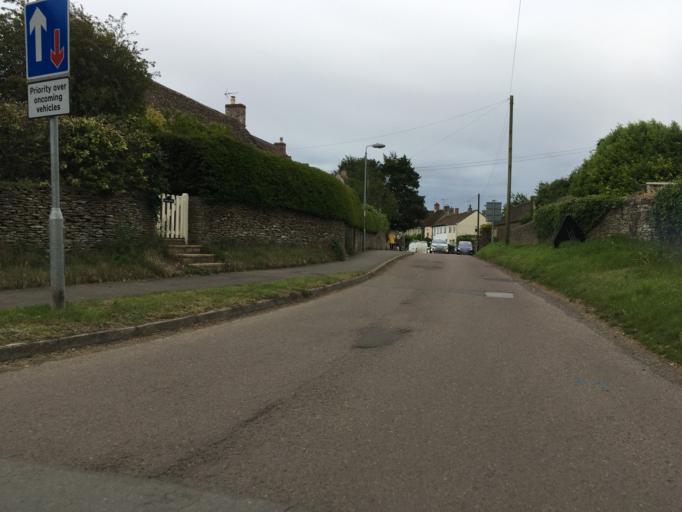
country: GB
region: England
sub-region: Wiltshire
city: Luckington
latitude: 51.5731
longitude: -2.2159
